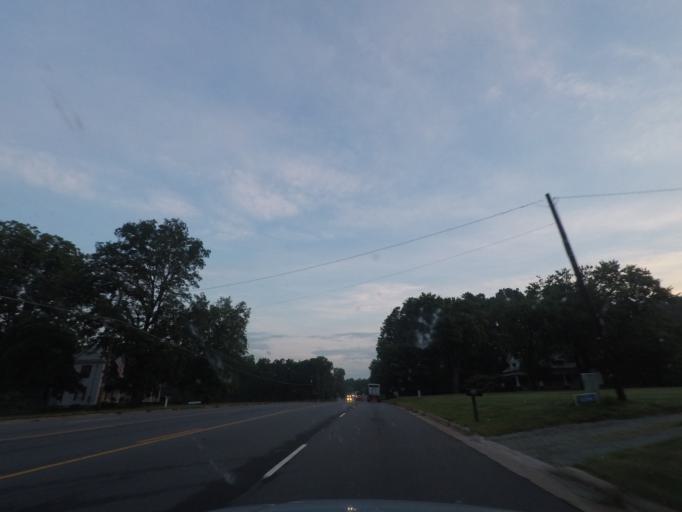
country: US
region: North Carolina
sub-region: Granville County
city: Butner
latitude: 36.2145
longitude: -78.9237
